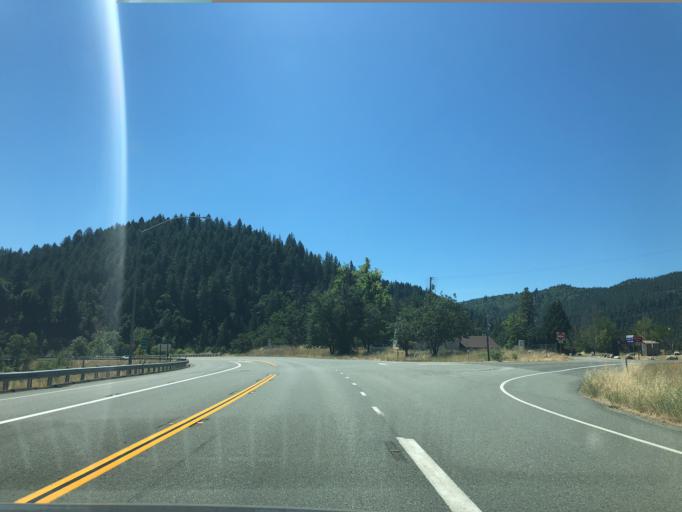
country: US
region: California
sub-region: Trinity County
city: Weaverville
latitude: 40.6537
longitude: -122.9428
